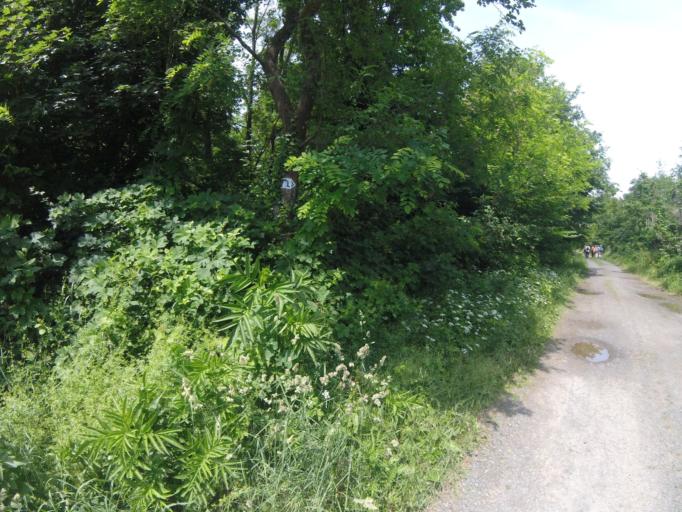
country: HU
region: Zala
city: Turje
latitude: 46.9094
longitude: 17.1824
